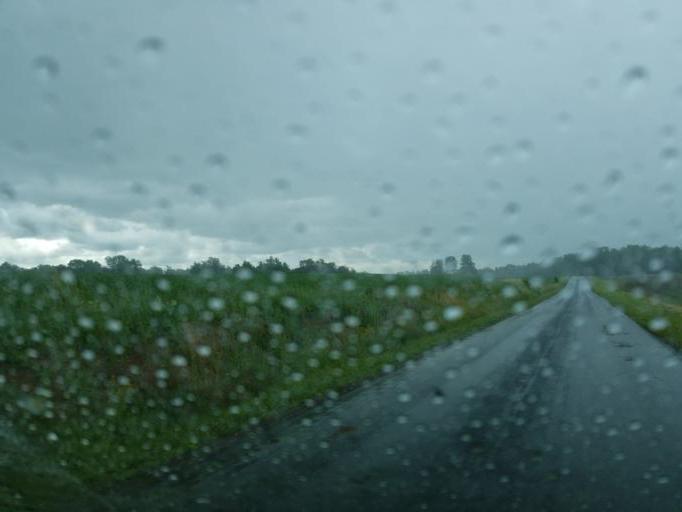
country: US
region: New York
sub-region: Wayne County
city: Clyde
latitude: 43.0311
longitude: -76.8828
